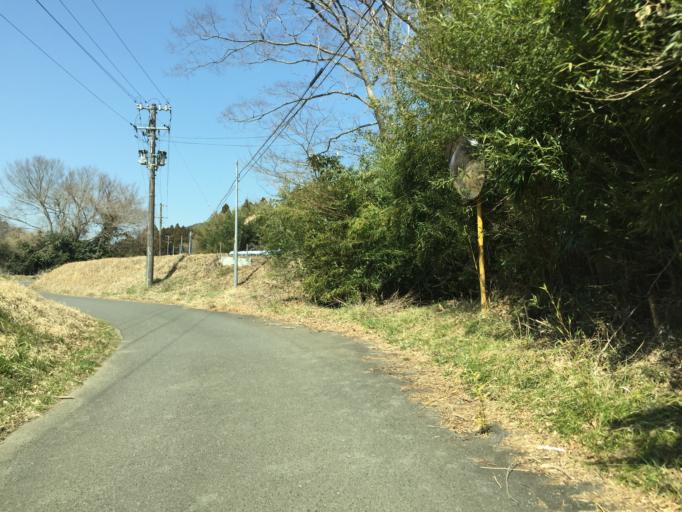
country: JP
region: Fukushima
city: Iwaki
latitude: 37.0114
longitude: 140.7897
